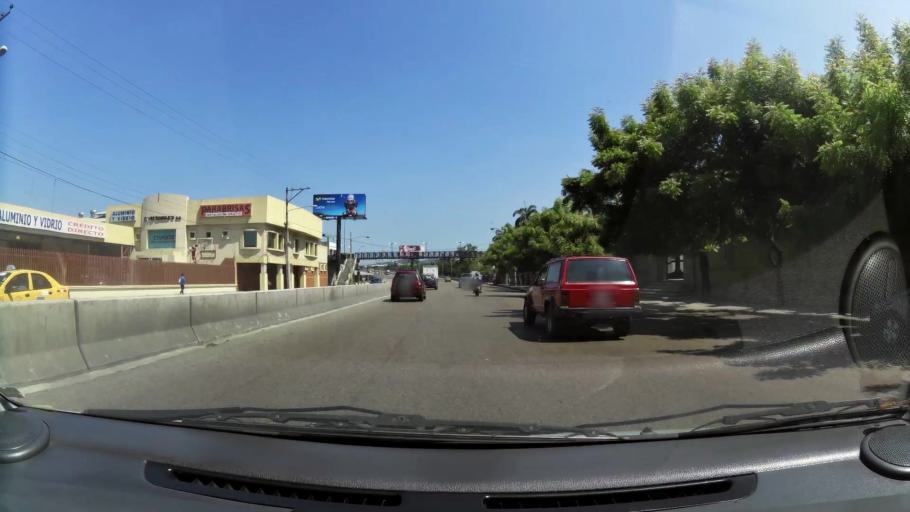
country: EC
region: Guayas
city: Eloy Alfaro
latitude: -2.1837
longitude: -79.8853
